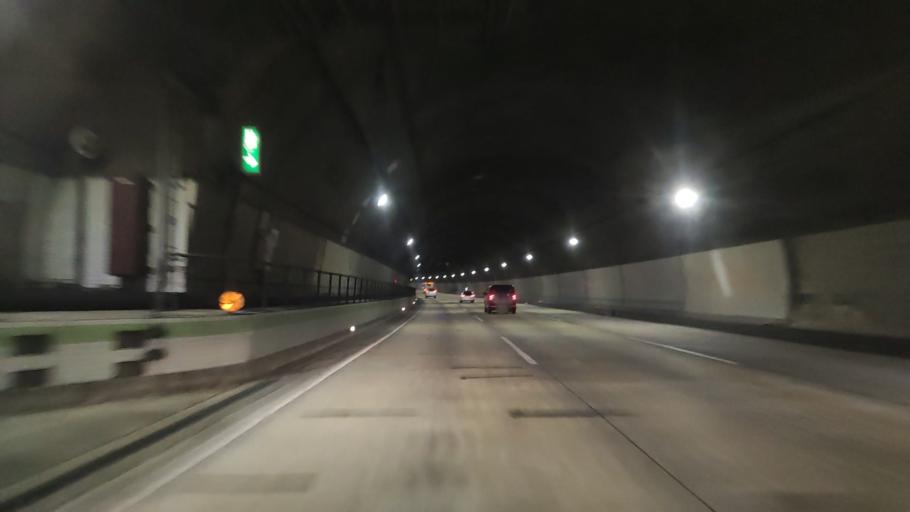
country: JP
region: Hyogo
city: Akashi
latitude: 34.6426
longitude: 135.0473
